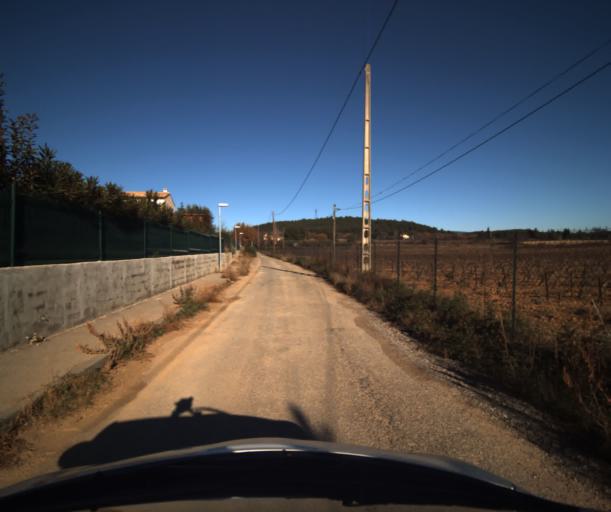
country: FR
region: Provence-Alpes-Cote d'Azur
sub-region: Departement du Vaucluse
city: Pertuis
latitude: 43.7072
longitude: 5.4996
